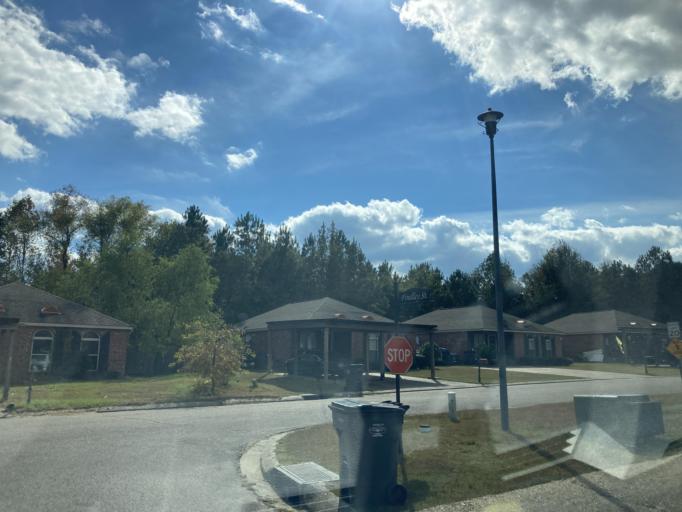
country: US
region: Mississippi
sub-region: Lamar County
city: Arnold Line
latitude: 31.3425
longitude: -89.3932
